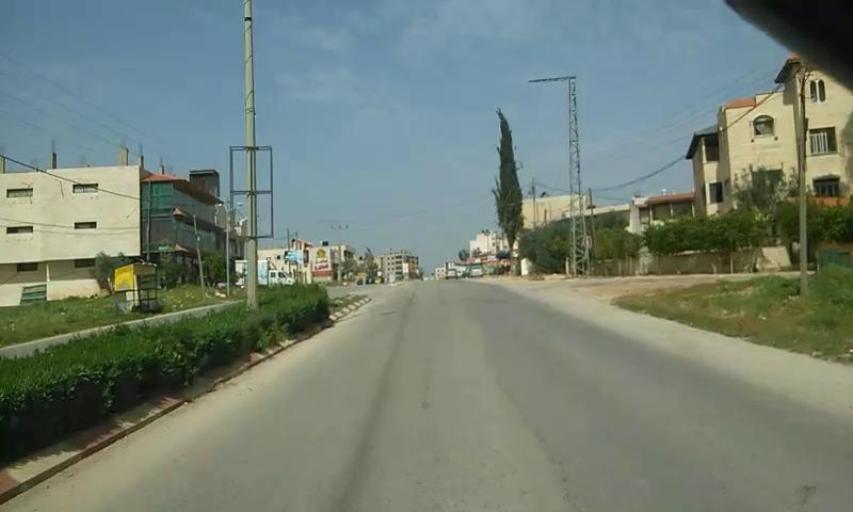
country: PS
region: West Bank
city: Janin
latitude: 32.4834
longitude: 35.2995
